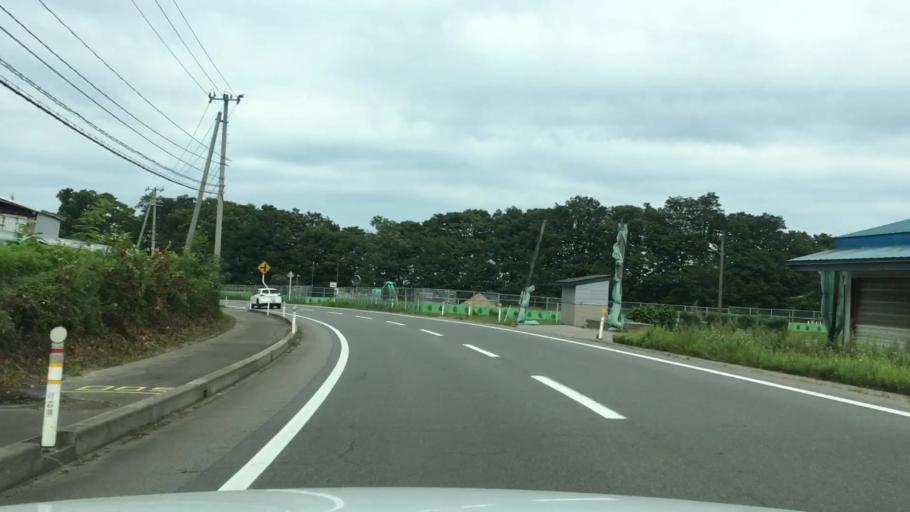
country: JP
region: Aomori
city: Shimokizukuri
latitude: 40.7661
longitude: 140.2245
